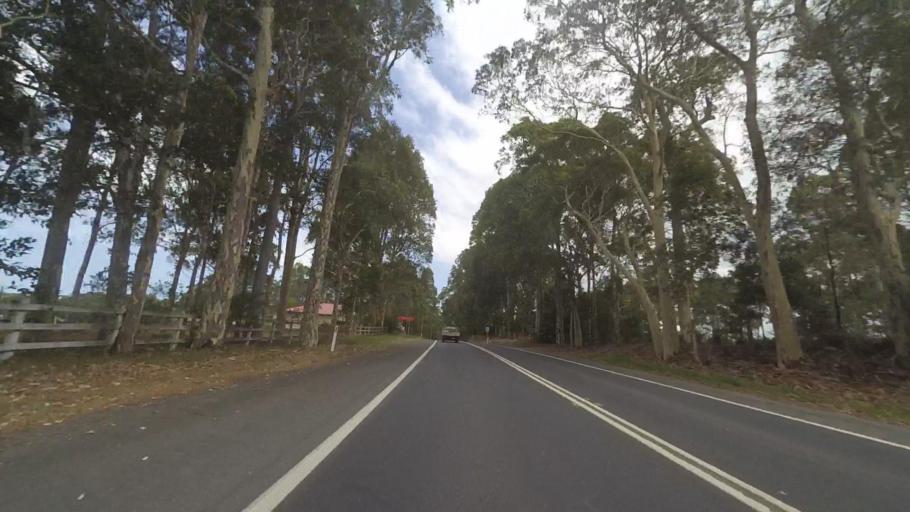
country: AU
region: New South Wales
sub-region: Shoalhaven Shire
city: Falls Creek
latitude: -35.0828
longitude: 150.5175
